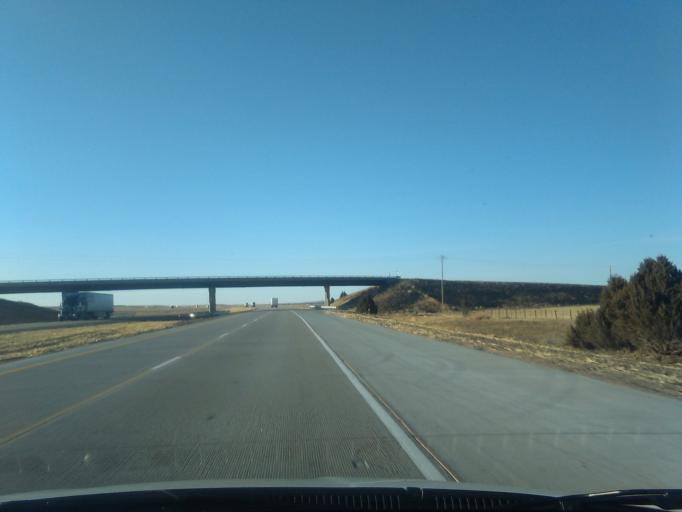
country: US
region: Nebraska
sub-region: Deuel County
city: Chappell
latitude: 41.1074
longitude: -102.5515
